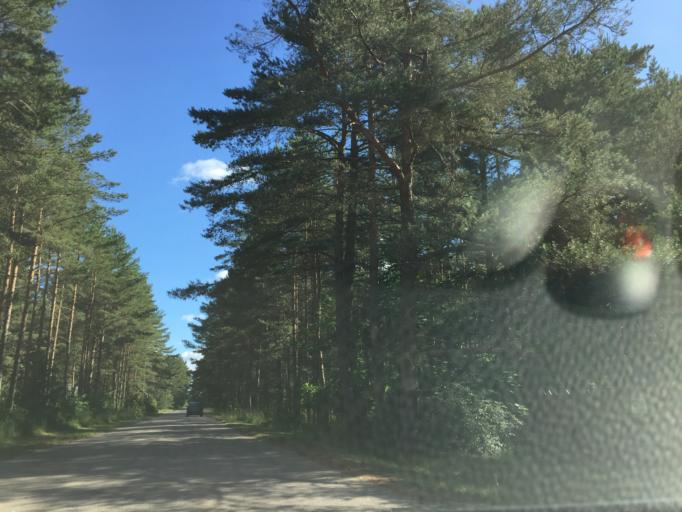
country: LV
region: Ventspils
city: Ventspils
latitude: 57.4461
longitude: 21.6227
